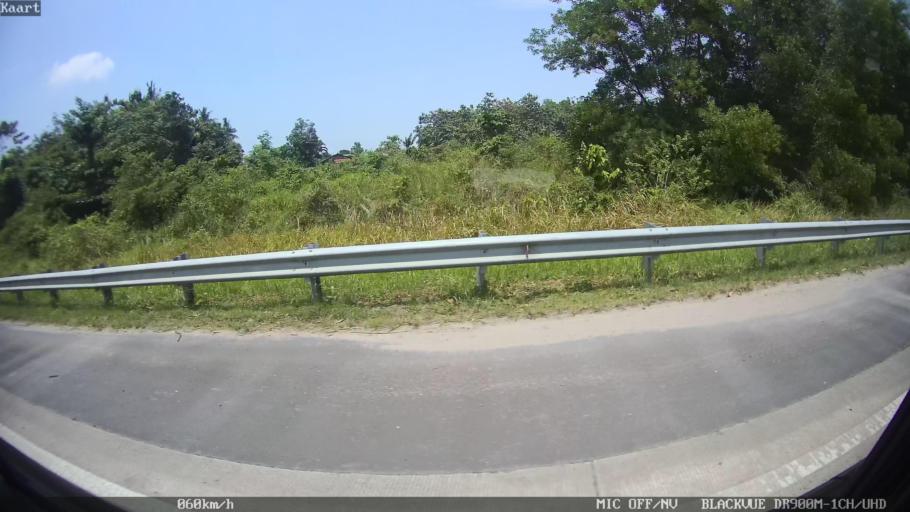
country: ID
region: Lampung
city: Kedaton
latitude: -5.3837
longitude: 105.3357
